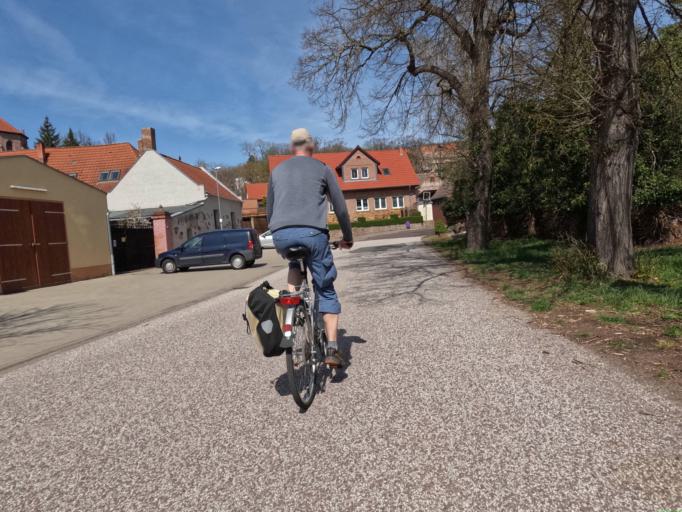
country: DE
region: Saxony-Anhalt
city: Beesenstedt
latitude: 51.6204
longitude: 11.7444
